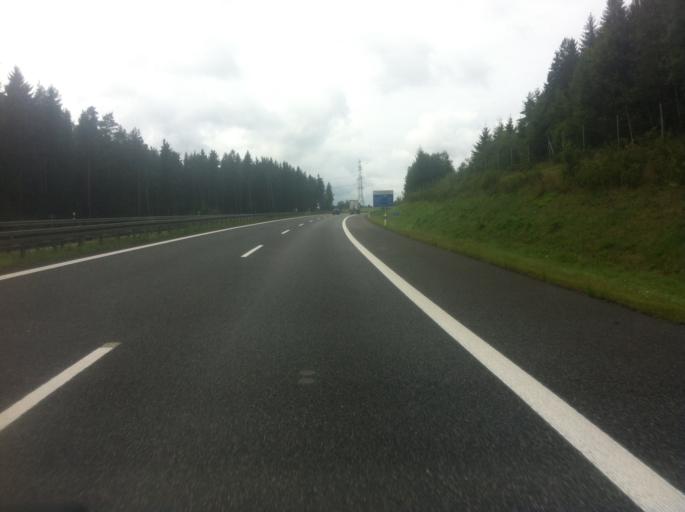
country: DE
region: Bavaria
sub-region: Upper Palatinate
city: Moosbach
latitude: 49.6138
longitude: 12.4082
